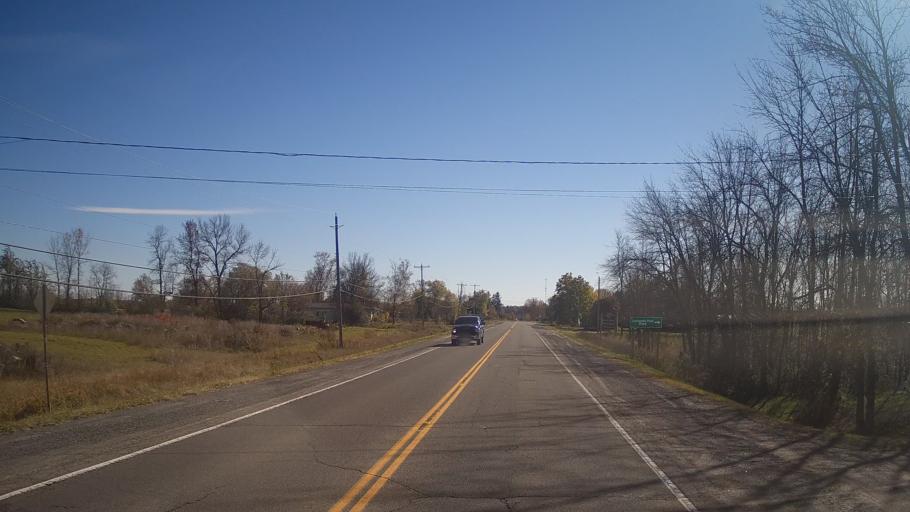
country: CA
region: Ontario
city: Kingston
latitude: 44.4135
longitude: -76.6663
